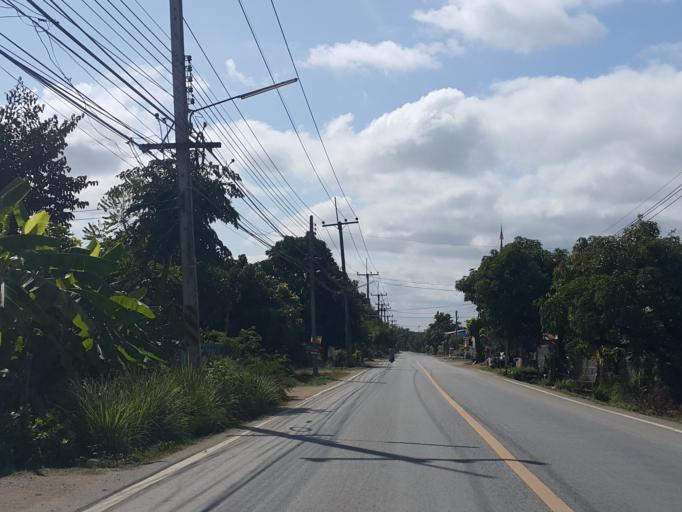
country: TH
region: Lamphun
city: Ban Thi
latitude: 18.6874
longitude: 99.1557
